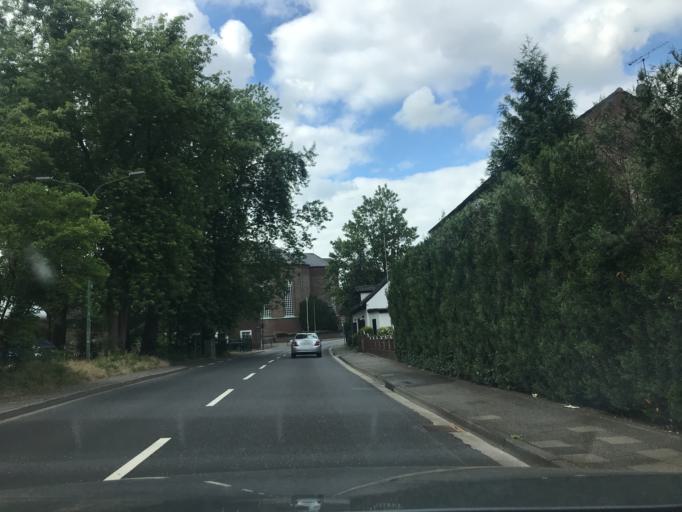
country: DE
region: North Rhine-Westphalia
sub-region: Regierungsbezirk Dusseldorf
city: Neuss
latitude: 51.1319
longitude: 6.7278
